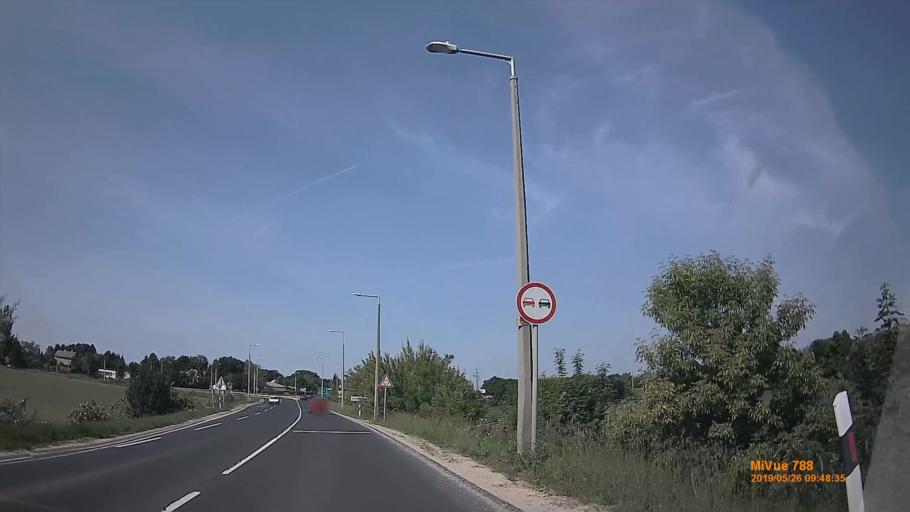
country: HU
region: Veszprem
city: Balatonkenese
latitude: 47.0165
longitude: 18.1704
